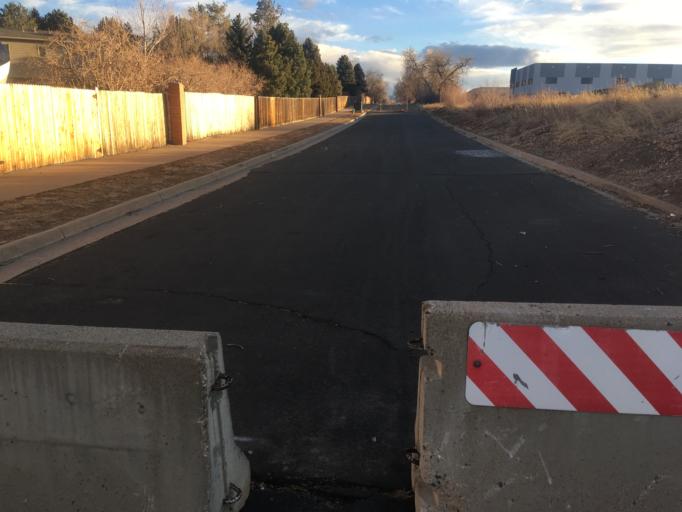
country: US
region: Colorado
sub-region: Jefferson County
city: Applewood
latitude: 39.8206
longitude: -105.1566
